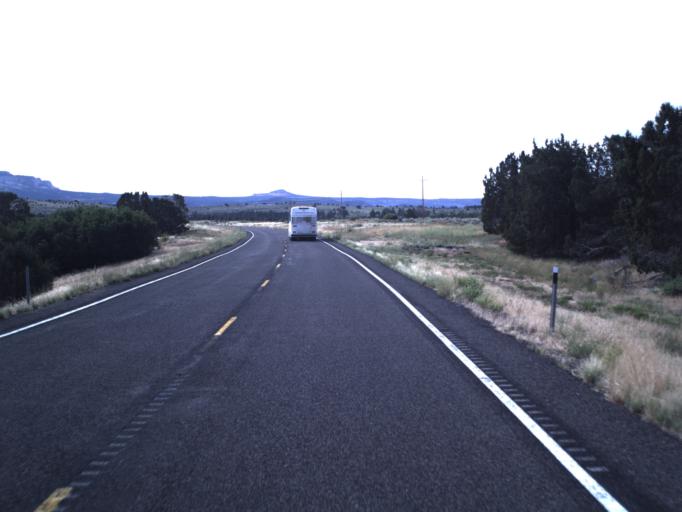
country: US
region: Utah
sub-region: Kane County
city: Kanab
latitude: 37.2399
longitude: -112.7495
